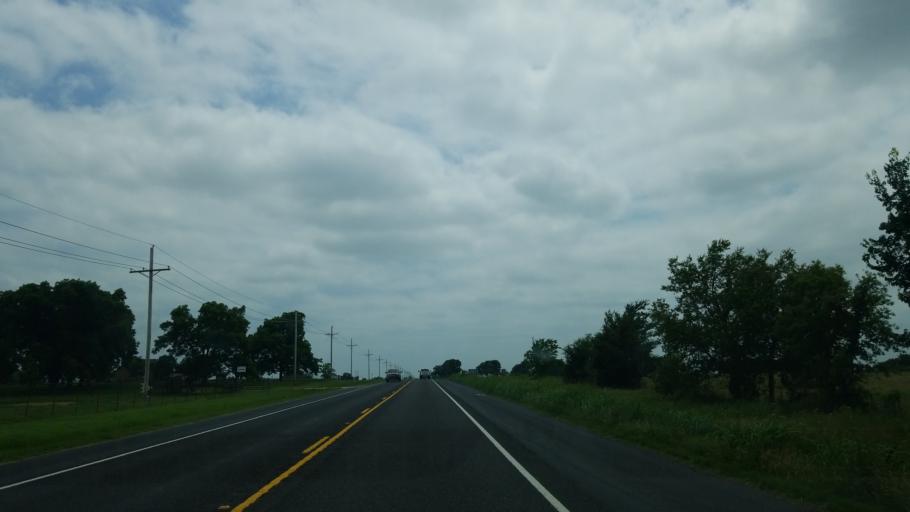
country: US
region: Texas
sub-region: Denton County
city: Pilot Point
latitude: 33.4298
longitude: -96.9323
